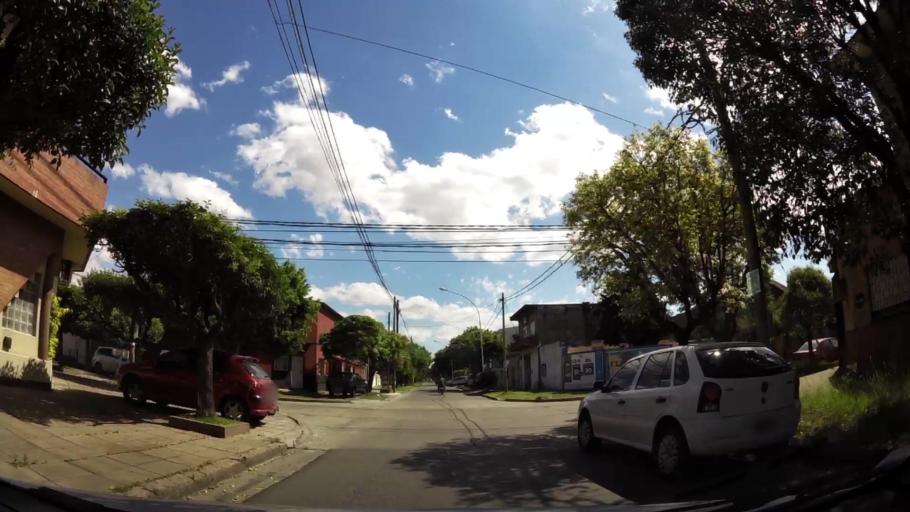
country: AR
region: Buenos Aires
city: San Justo
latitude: -34.6588
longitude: -58.5333
